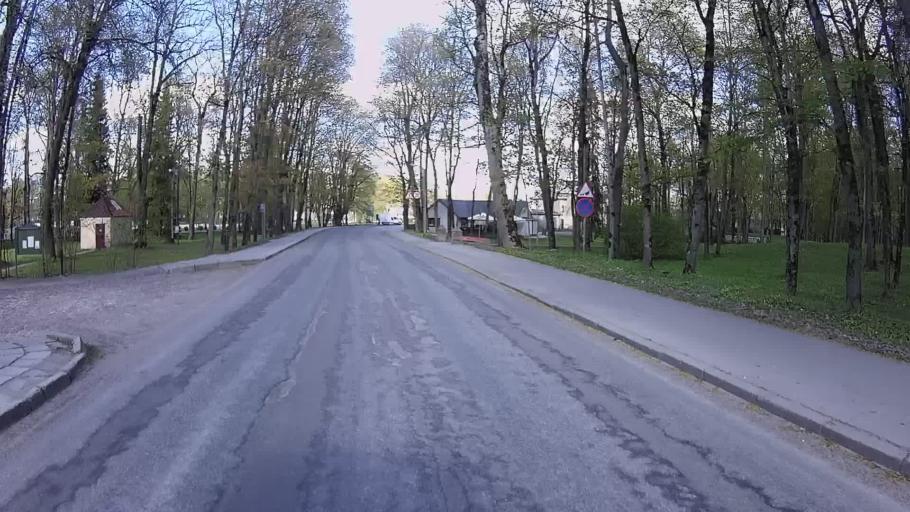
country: EE
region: Jogevamaa
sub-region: Poltsamaa linn
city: Poltsamaa
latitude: 58.6538
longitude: 25.9693
